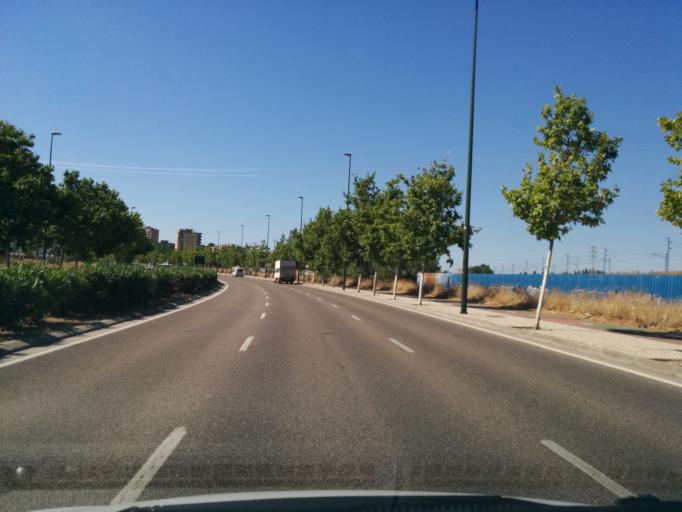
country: ES
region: Aragon
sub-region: Provincia de Zaragoza
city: Zaragoza
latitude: 41.6578
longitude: -0.8531
